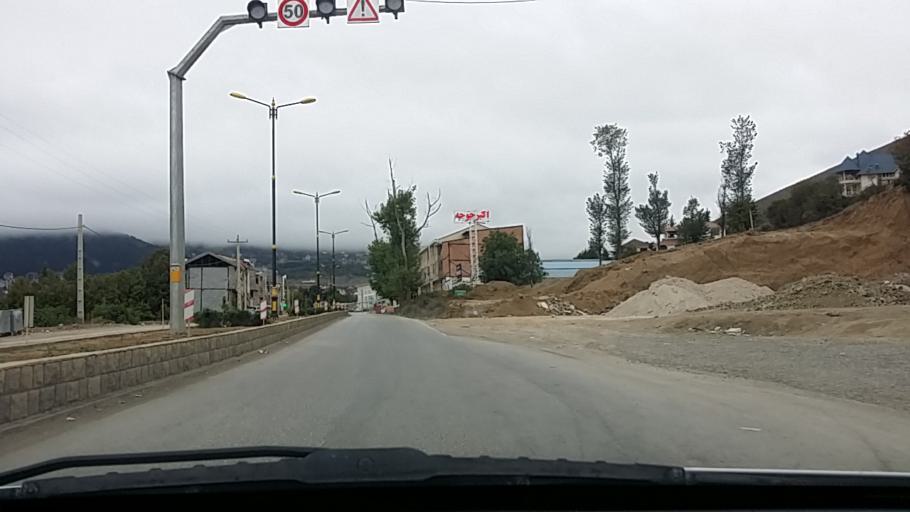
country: IR
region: Mazandaran
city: `Abbasabad
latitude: 36.5127
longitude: 51.1595
